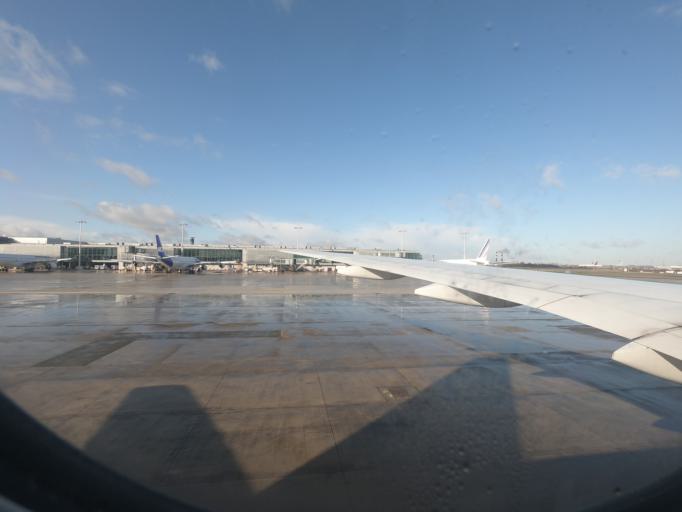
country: FR
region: Ile-de-France
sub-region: Departement de Seine-et-Marne
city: Mitry-Mory
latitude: 49.0068
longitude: 2.5882
